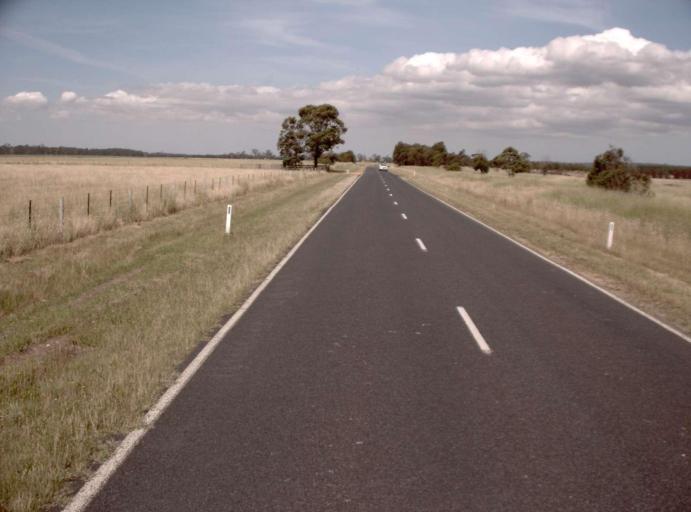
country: AU
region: Victoria
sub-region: Wellington
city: Heyfield
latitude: -38.1551
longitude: 146.8396
